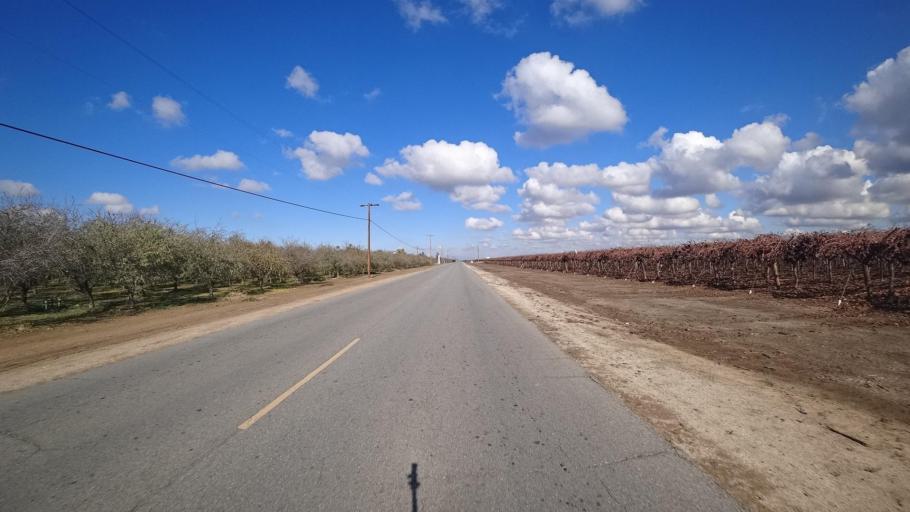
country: US
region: California
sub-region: Kern County
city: McFarland
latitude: 35.6652
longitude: -119.2047
